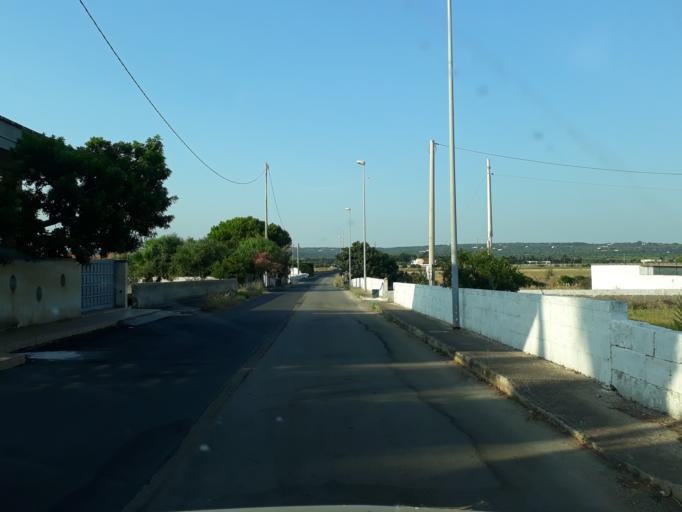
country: IT
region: Apulia
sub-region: Provincia di Brindisi
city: Carovigno
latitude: 40.7517
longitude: 17.7053
